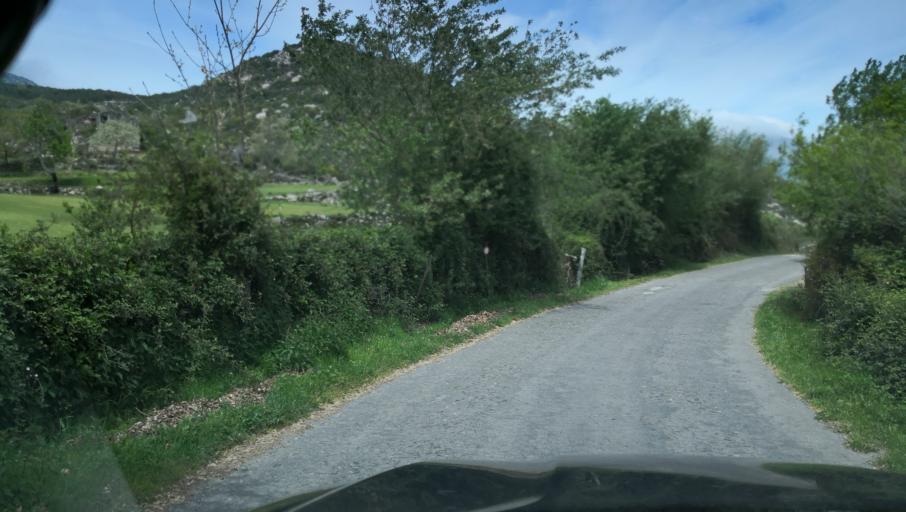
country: PT
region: Vila Real
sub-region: Vila Real
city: Vila Real
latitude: 41.2939
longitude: -7.8052
